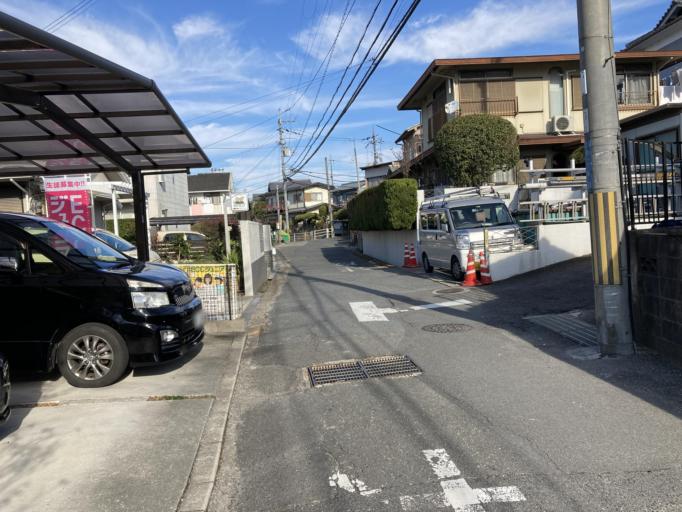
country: JP
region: Nara
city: Nara-shi
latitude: 34.6691
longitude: 135.7772
